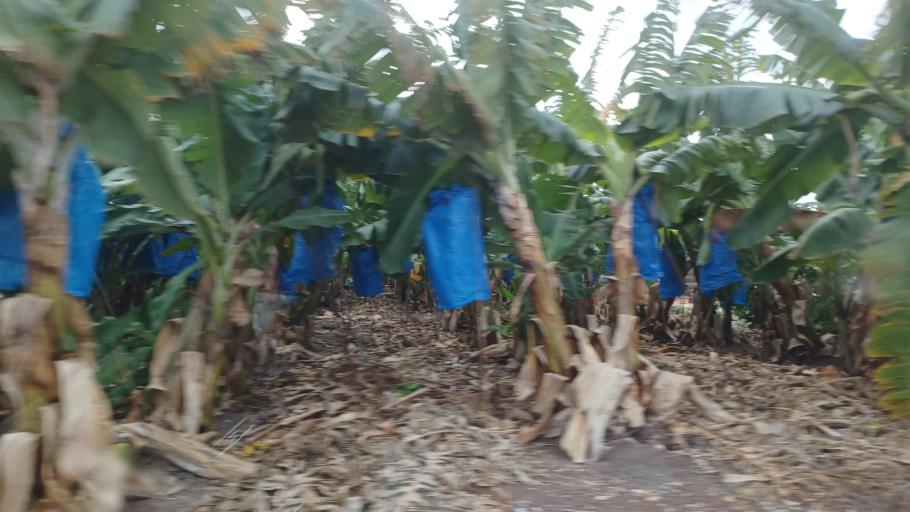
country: CY
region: Pafos
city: Pegeia
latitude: 34.8967
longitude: 32.3358
